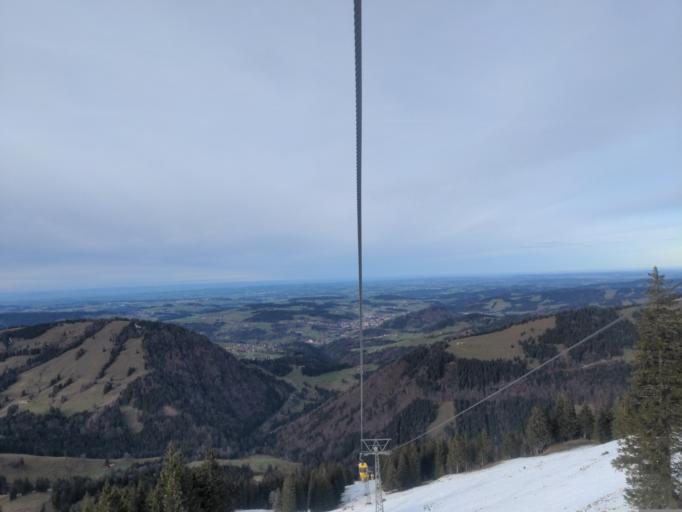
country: DE
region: Bavaria
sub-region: Swabia
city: Balderschwang
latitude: 47.4955
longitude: 10.0699
